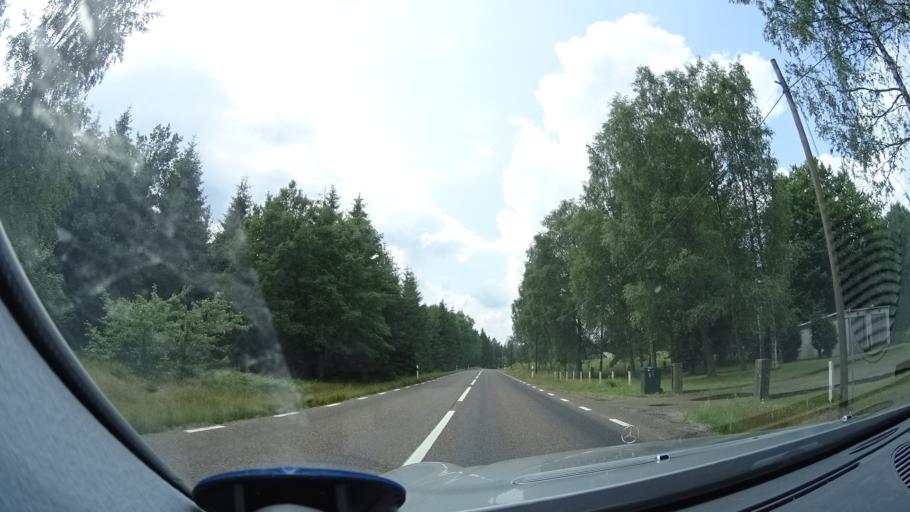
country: SE
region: Kalmar
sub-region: Emmaboda Kommun
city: Emmaboda
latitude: 56.6296
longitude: 15.6378
